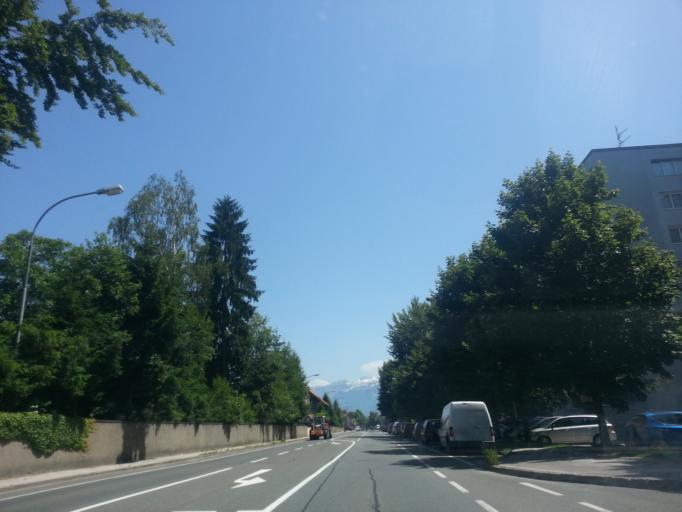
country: AT
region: Salzburg
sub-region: Politischer Bezirk Hallein
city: Hallein
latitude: 47.6815
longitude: 13.1022
